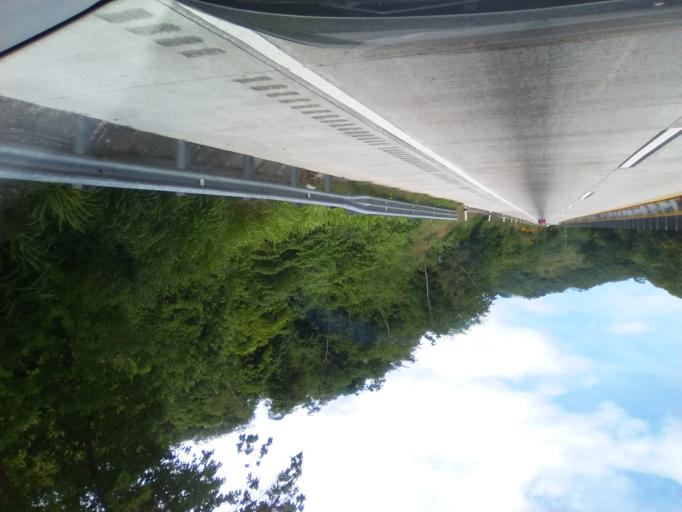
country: MX
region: Guerrero
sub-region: Chilpancingo de los Bravo
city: Julian Blanco (Dos Caminos)
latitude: 17.1949
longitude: -99.5323
